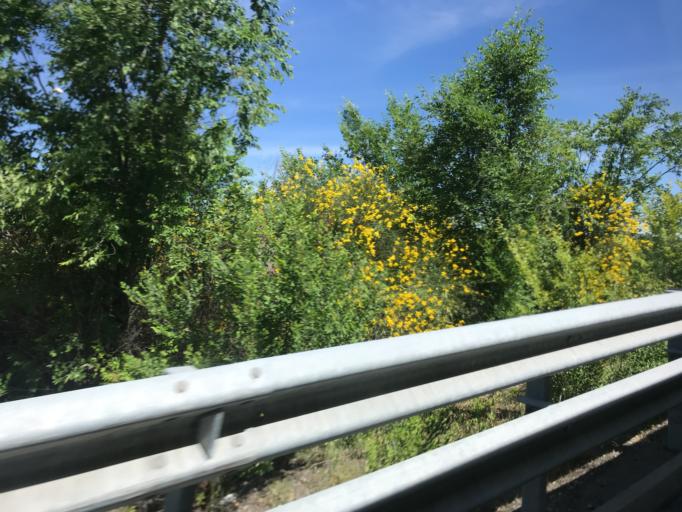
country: ES
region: Madrid
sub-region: Provincia de Madrid
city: Vicalvaro
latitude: 40.4128
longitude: -3.6179
